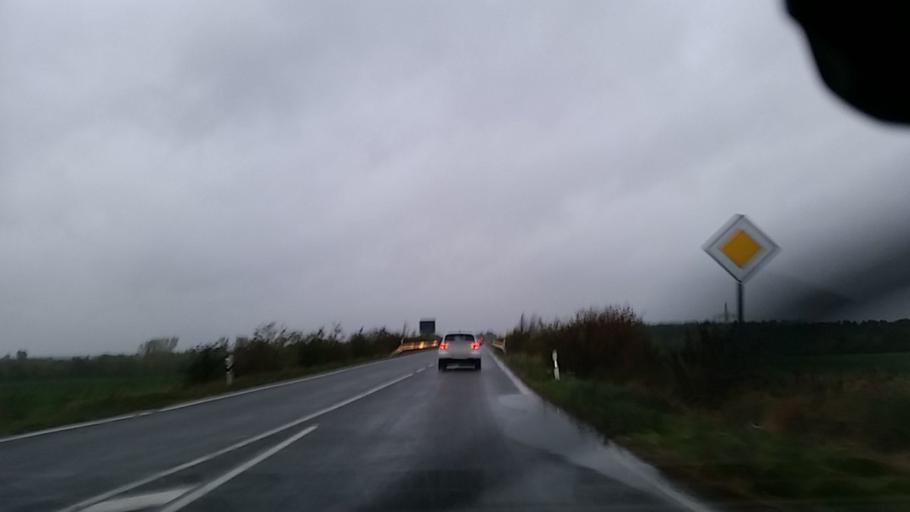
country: DE
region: Lower Saxony
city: Calberlah
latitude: 52.4180
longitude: 10.6719
